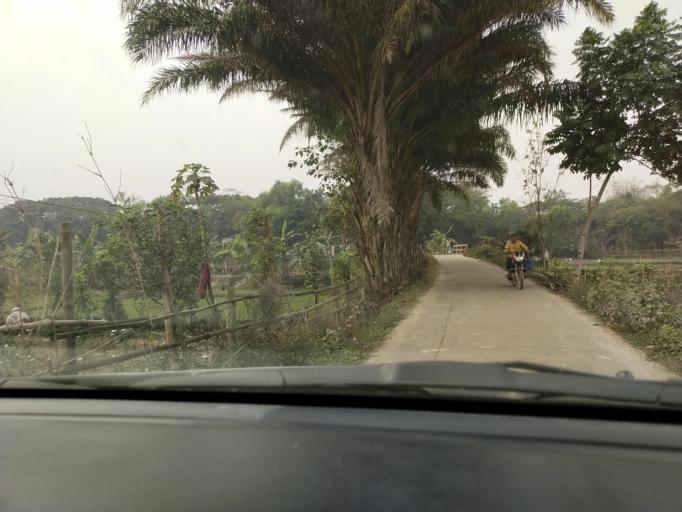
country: BD
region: Dhaka
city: Narsingdi
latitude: 24.0349
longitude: 90.7201
